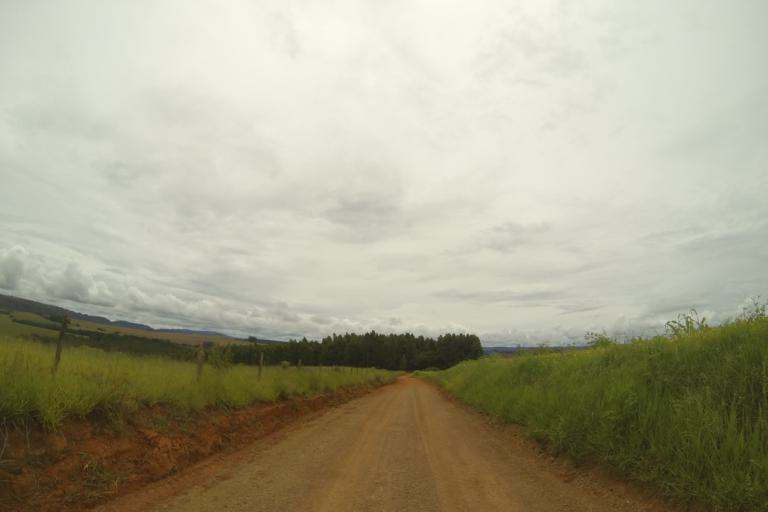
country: BR
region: Minas Gerais
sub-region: Ibia
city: Ibia
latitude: -19.7413
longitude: -46.6360
